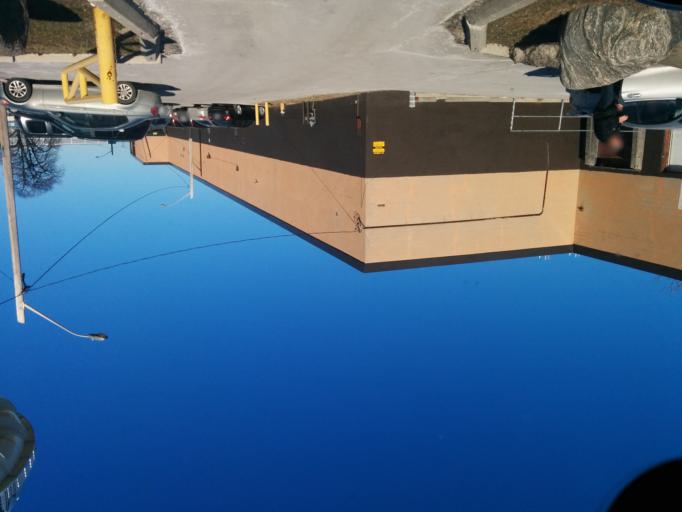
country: CA
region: Ontario
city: Etobicoke
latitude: 43.6023
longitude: -79.5234
